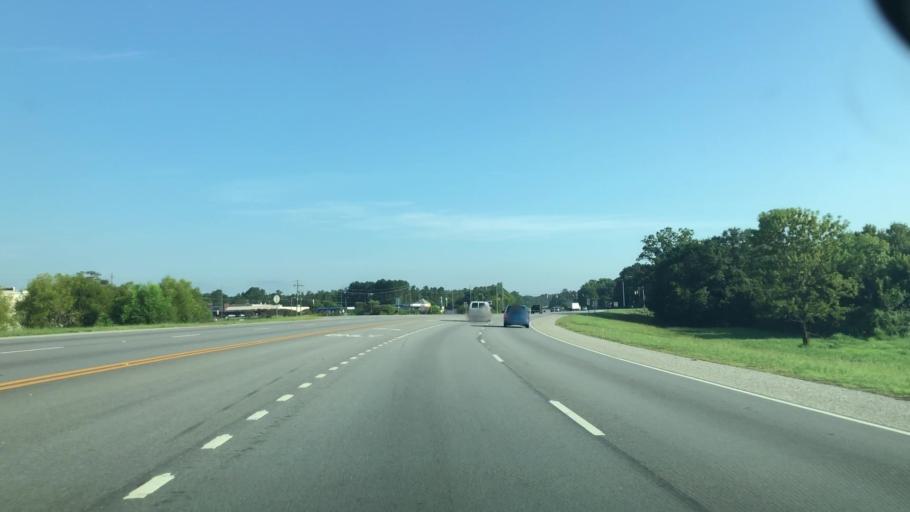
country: US
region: Alabama
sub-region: Calhoun County
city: Bynum
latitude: 33.5935
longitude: -85.9246
